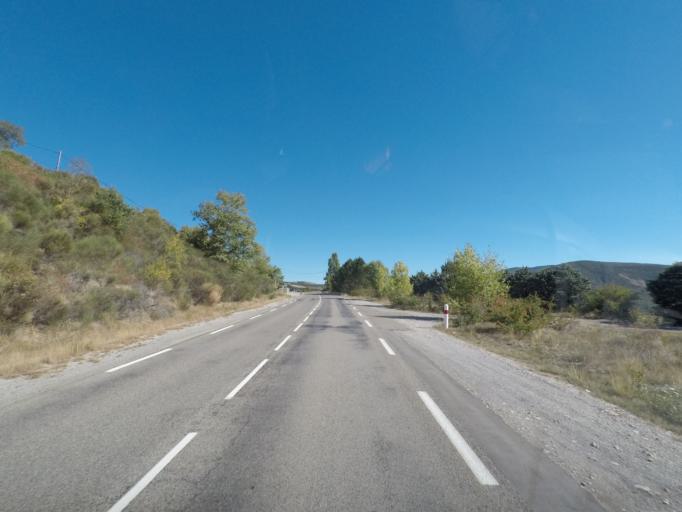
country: FR
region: Provence-Alpes-Cote d'Azur
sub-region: Departement des Hautes-Alpes
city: Serres
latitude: 44.3888
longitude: 5.4817
